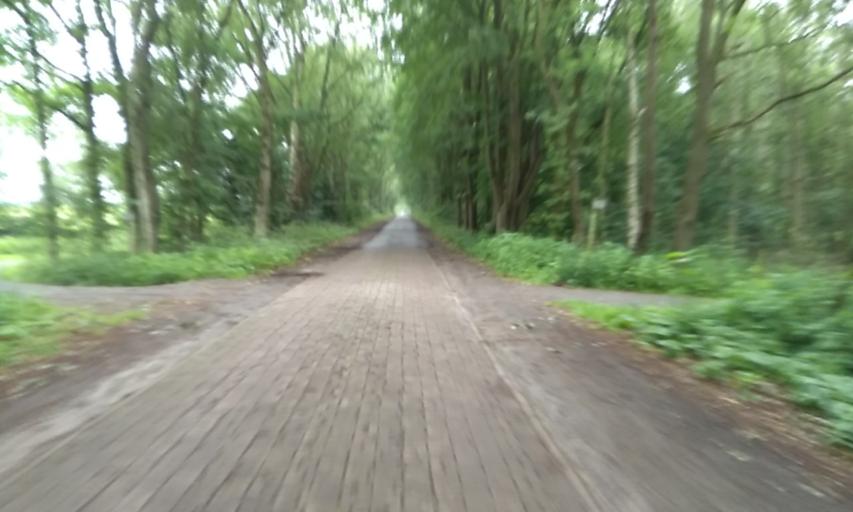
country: DE
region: Lower Saxony
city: Deinste
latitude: 53.5389
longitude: 9.4292
